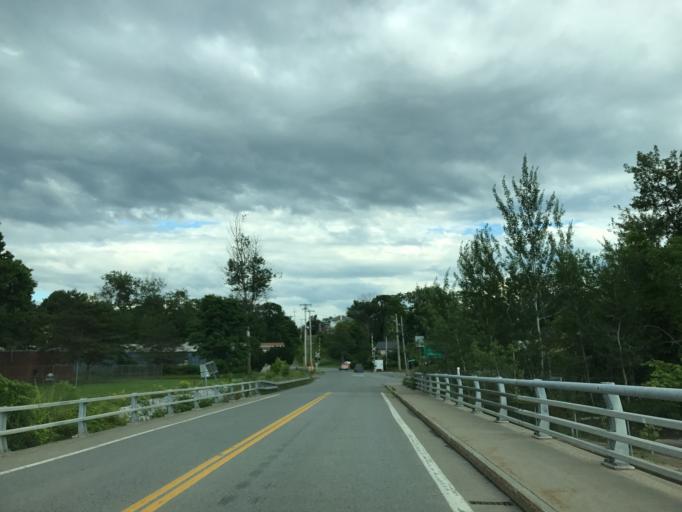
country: US
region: New York
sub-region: Washington County
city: Hudson Falls
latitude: 43.2976
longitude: -73.5888
